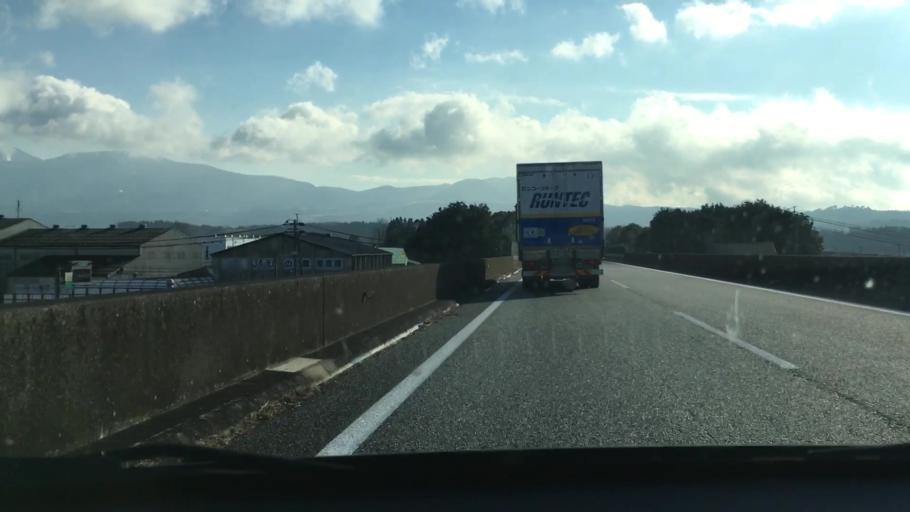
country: JP
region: Kumamoto
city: Hitoyoshi
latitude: 32.0537
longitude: 130.8021
